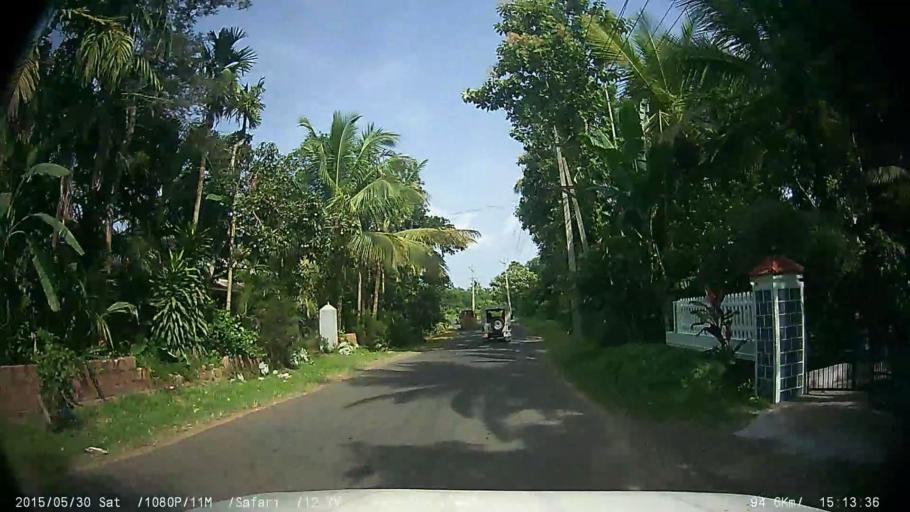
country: IN
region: Kerala
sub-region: Wayanad
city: Panamaram
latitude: 11.7902
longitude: 76.0434
